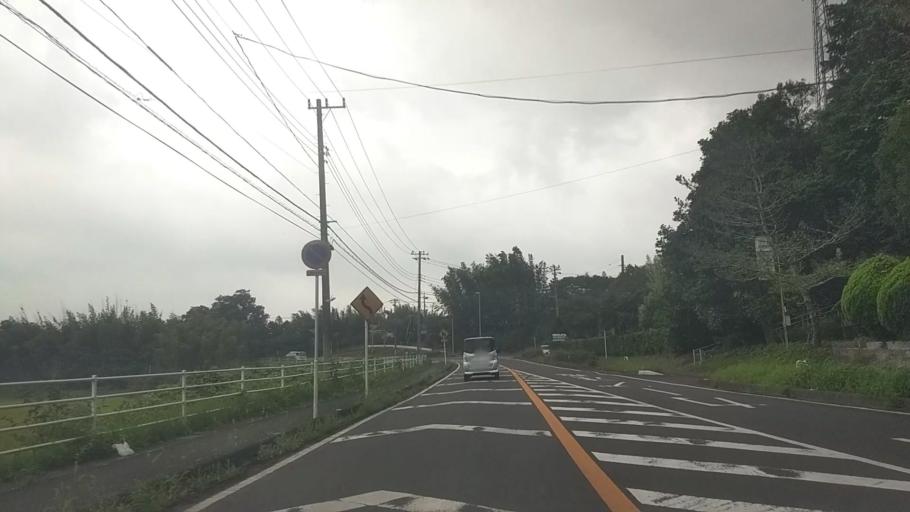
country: JP
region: Chiba
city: Ohara
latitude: 35.2829
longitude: 140.3203
